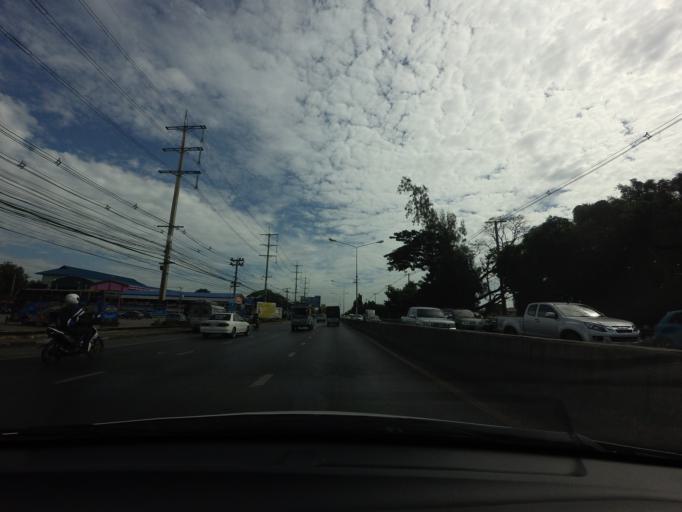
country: TH
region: Pathum Thani
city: Thanyaburi
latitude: 14.0209
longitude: 100.7364
